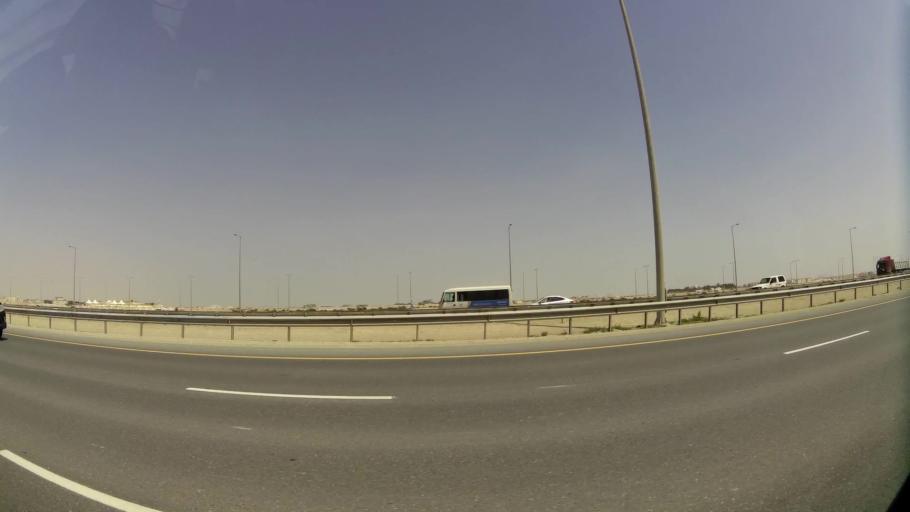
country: QA
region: Baladiyat Umm Salal
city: Umm Salal Muhammad
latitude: 25.4250
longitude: 51.4176
